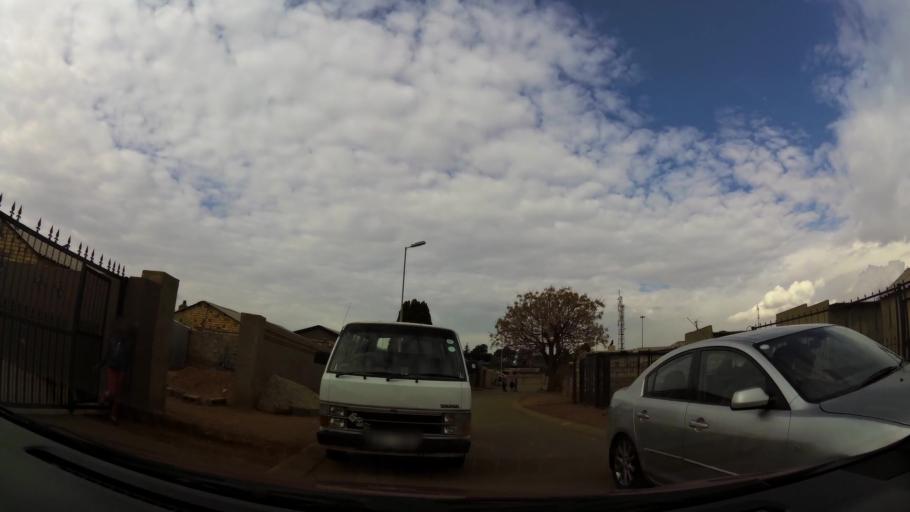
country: ZA
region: Gauteng
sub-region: City of Johannesburg Metropolitan Municipality
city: Soweto
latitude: -26.2447
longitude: 27.8537
